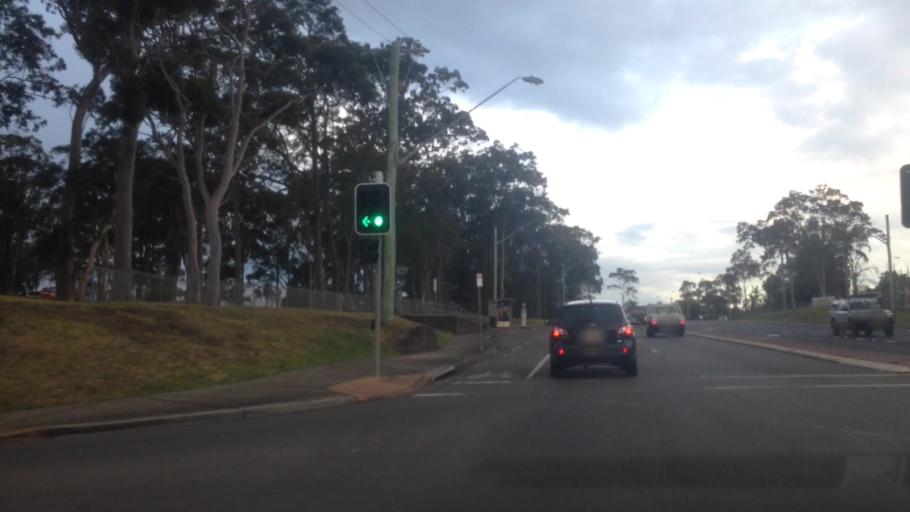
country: AU
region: New South Wales
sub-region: Wyong Shire
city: Kanwal
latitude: -33.2624
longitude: 151.4815
